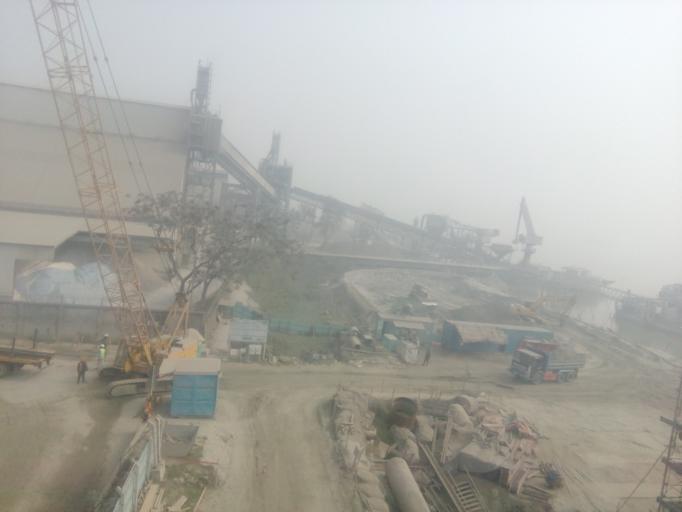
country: BD
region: Dhaka
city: Narayanganj
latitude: 23.6094
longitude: 90.6123
